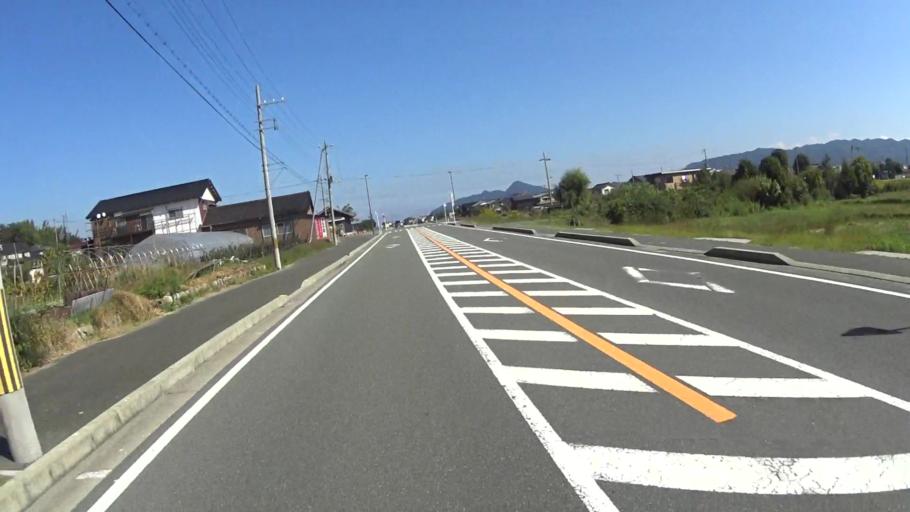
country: JP
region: Kyoto
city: Miyazu
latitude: 35.5857
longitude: 135.1890
